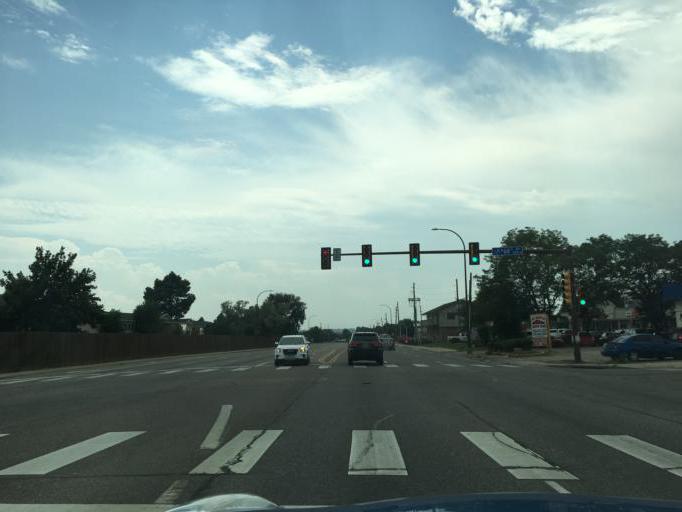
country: US
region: Colorado
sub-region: Jefferson County
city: Arvada
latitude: 39.8206
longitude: -105.0814
